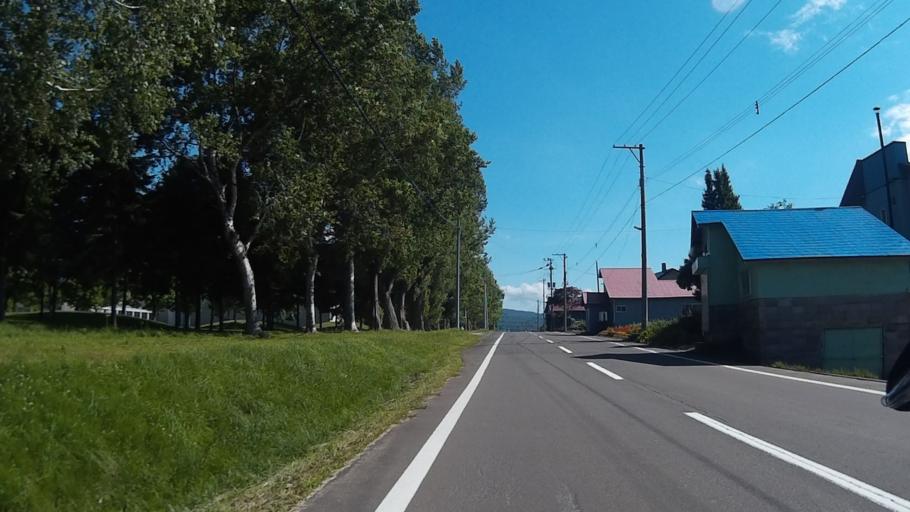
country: JP
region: Hokkaido
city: Niseko Town
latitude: 42.9077
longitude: 140.7668
